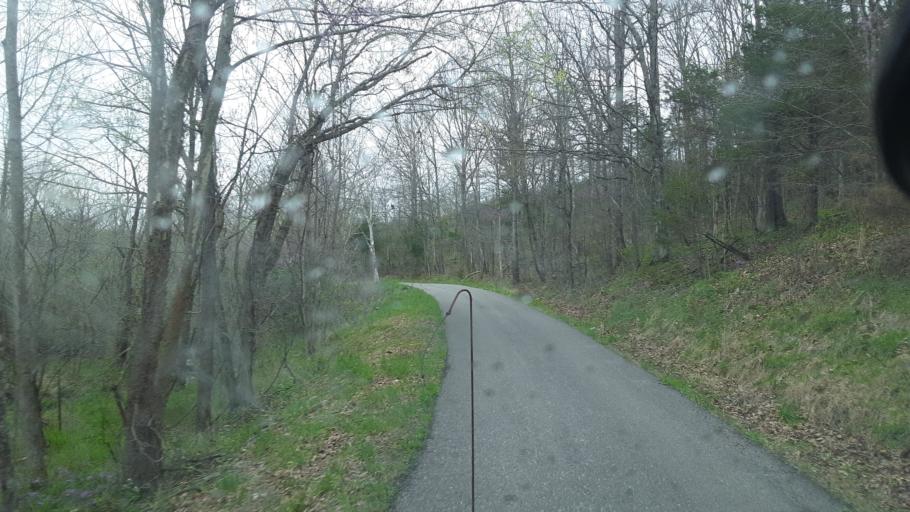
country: US
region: Kentucky
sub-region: Owen County
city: Owenton
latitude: 38.6447
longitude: -84.7838
